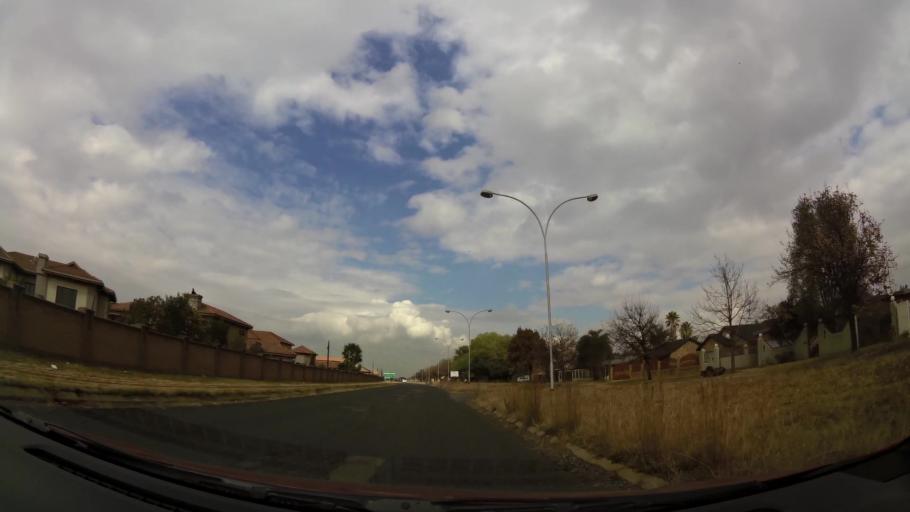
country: ZA
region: Gauteng
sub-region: Sedibeng District Municipality
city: Vanderbijlpark
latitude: -26.7251
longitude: 27.8628
